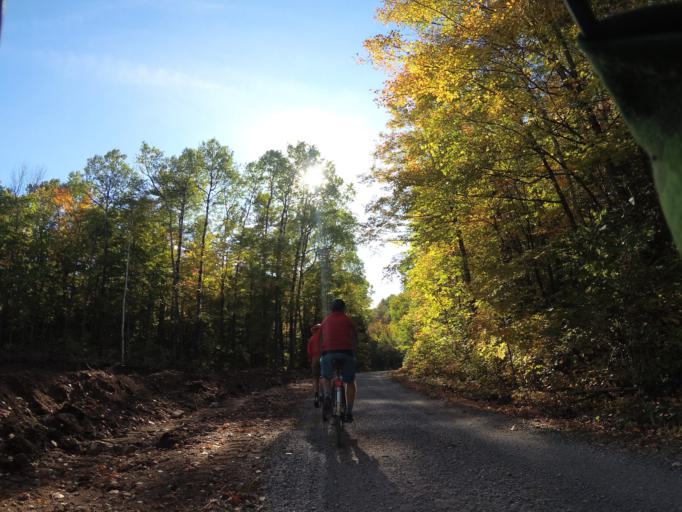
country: CA
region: Ontario
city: Pembroke
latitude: 45.3465
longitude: -77.1676
